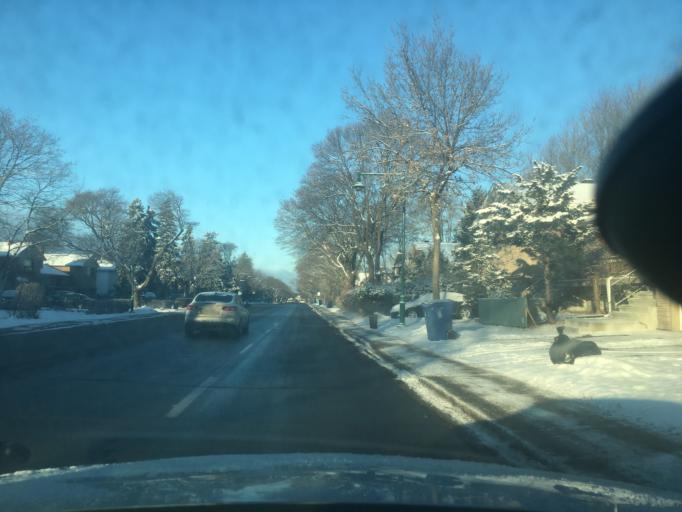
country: CA
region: Quebec
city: Mont-Royal
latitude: 45.5038
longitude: -73.6487
